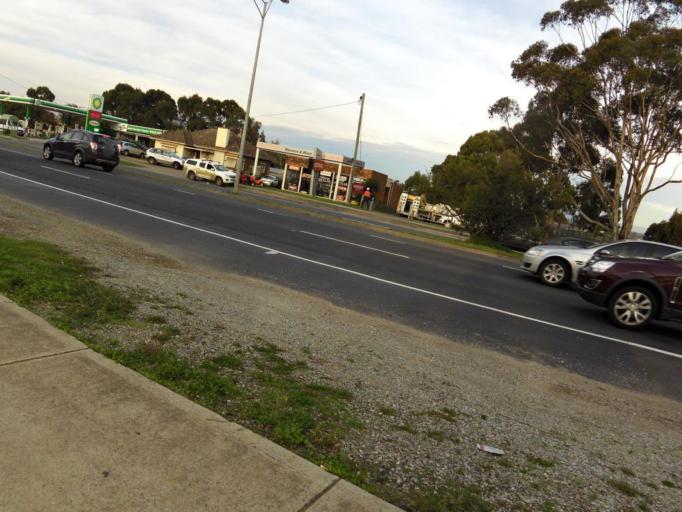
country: AU
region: Victoria
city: Plenty
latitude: -37.6805
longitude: 145.1220
